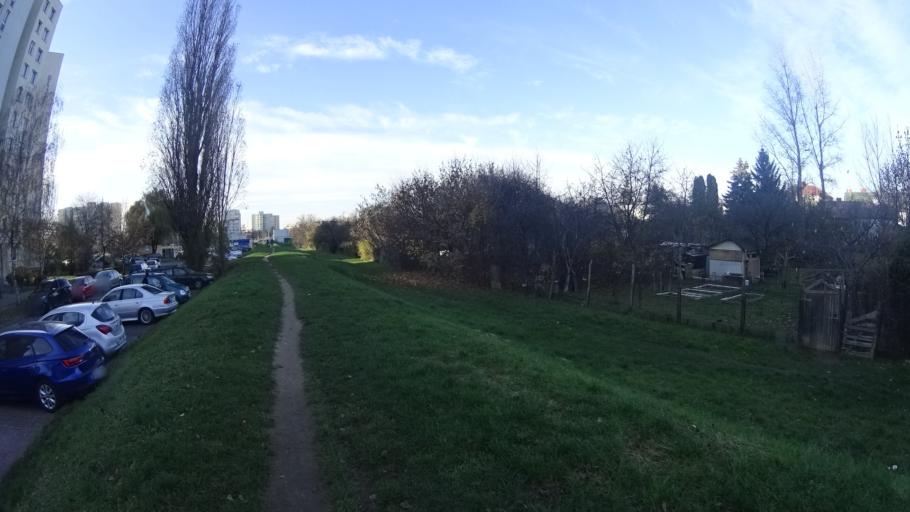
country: PL
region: Masovian Voivodeship
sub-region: Warszawa
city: Targowek
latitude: 52.2764
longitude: 21.0613
